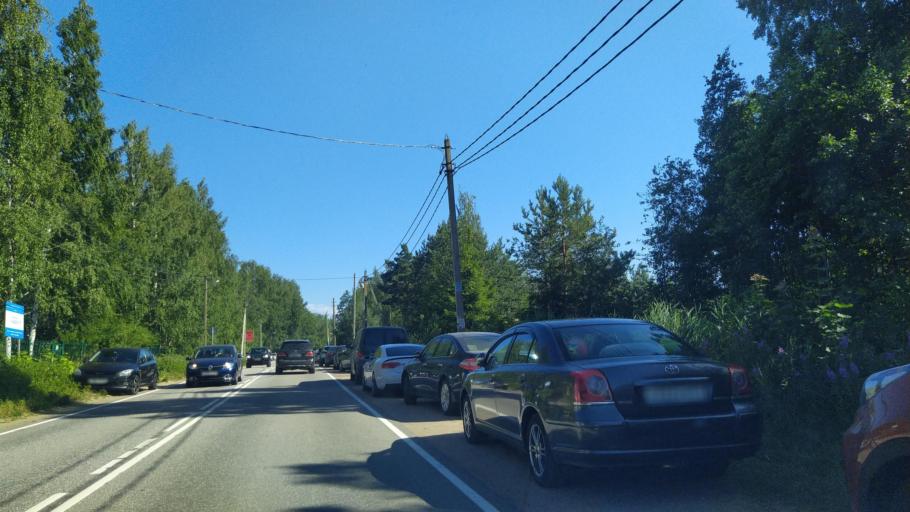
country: RU
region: Leningrad
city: Borisova Griva
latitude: 60.1162
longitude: 31.0813
